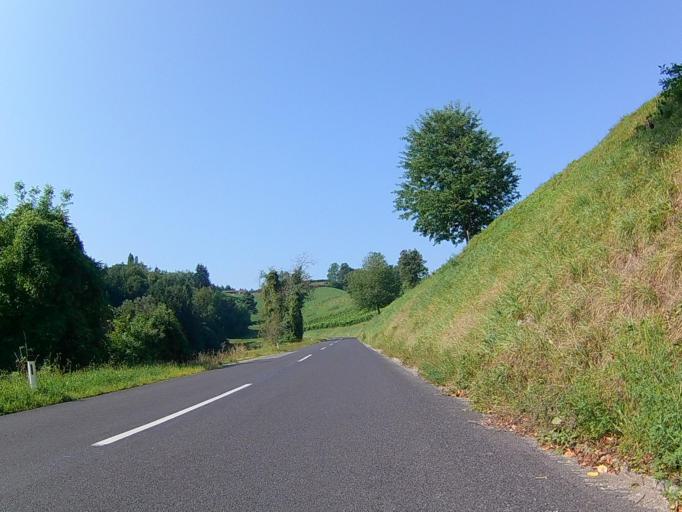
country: AT
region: Styria
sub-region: Politischer Bezirk Leibnitz
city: Sulztal an der Weinstrasse
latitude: 46.6461
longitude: 15.5197
